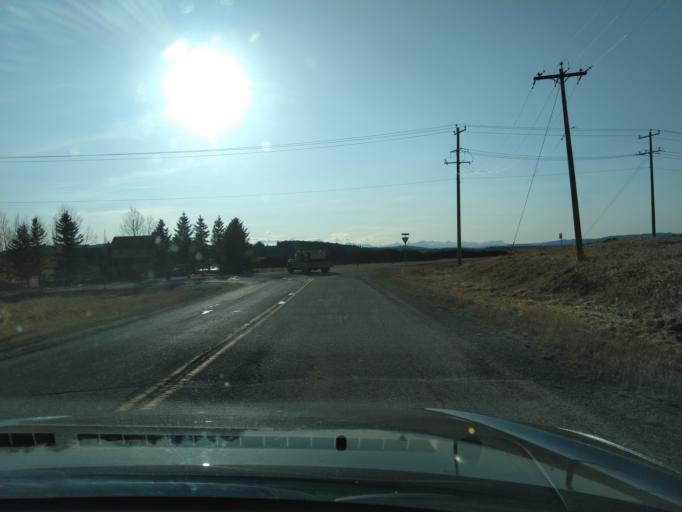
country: CA
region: Alberta
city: Cochrane
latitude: 51.1687
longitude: -114.4893
